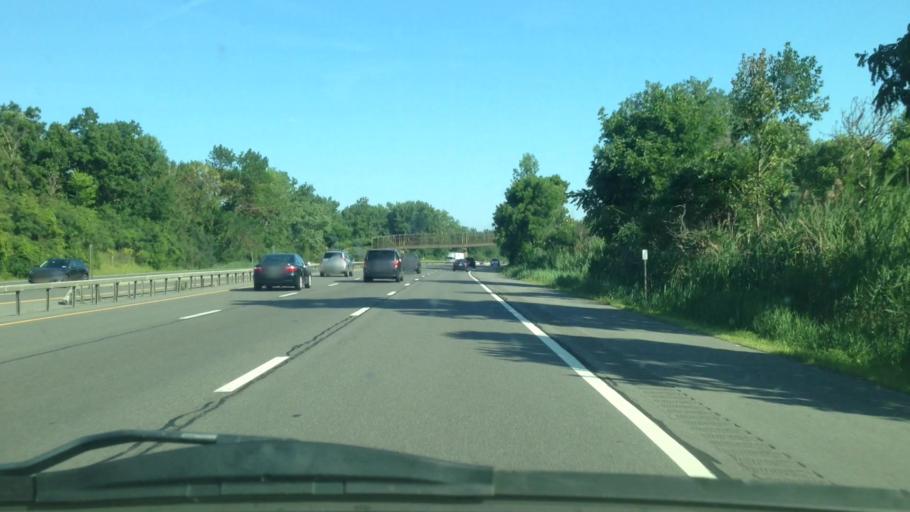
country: US
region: New York
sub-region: Onondaga County
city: Lakeland
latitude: 43.0945
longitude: -76.2365
